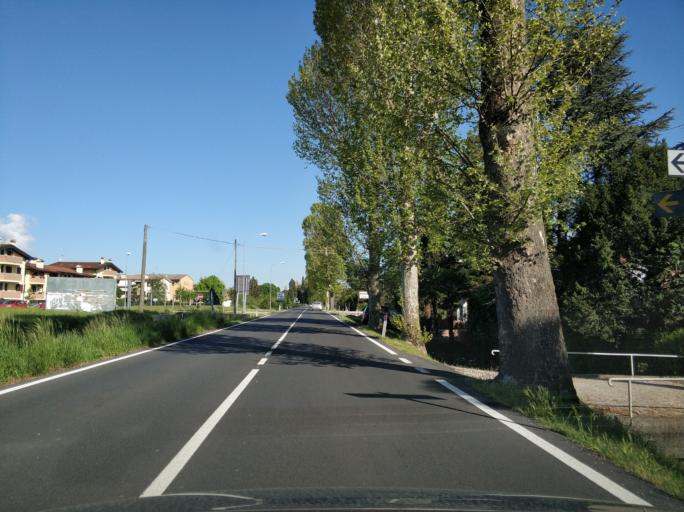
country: IT
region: Friuli Venezia Giulia
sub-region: Provincia di Udine
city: Terzo d'Aquileia
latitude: 45.8014
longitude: 13.3483
